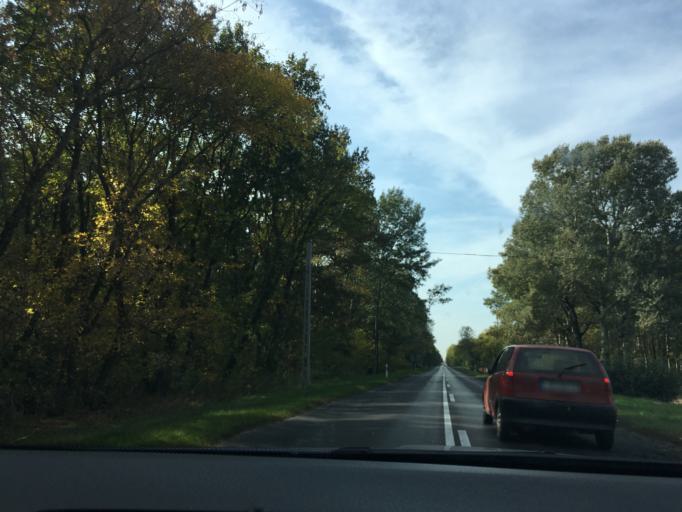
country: HU
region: Hajdu-Bihar
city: Hajdusamson
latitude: 47.5276
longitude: 21.7327
